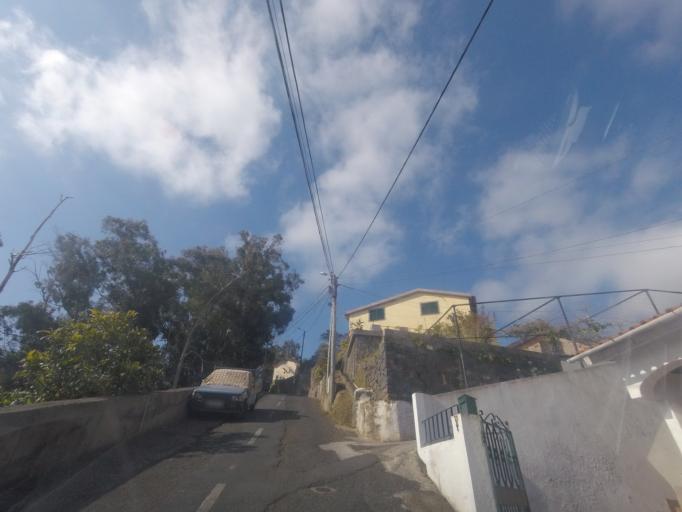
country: PT
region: Madeira
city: Camara de Lobos
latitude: 32.6756
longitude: -16.9539
